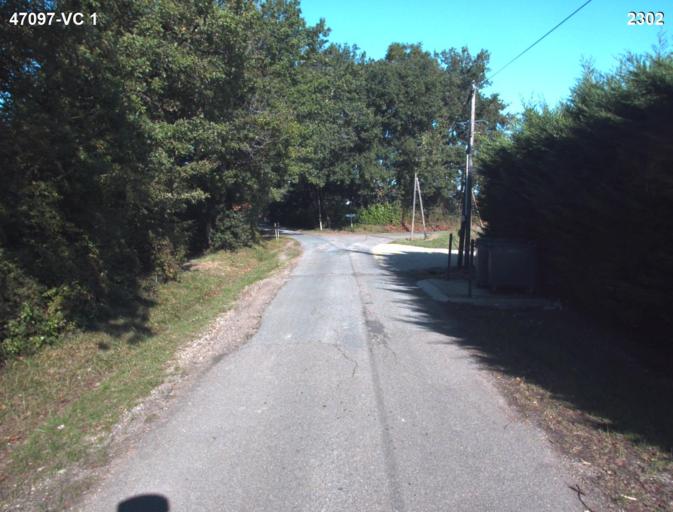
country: FR
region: Aquitaine
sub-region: Departement du Lot-et-Garonne
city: Vianne
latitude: 44.2055
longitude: 0.3581
